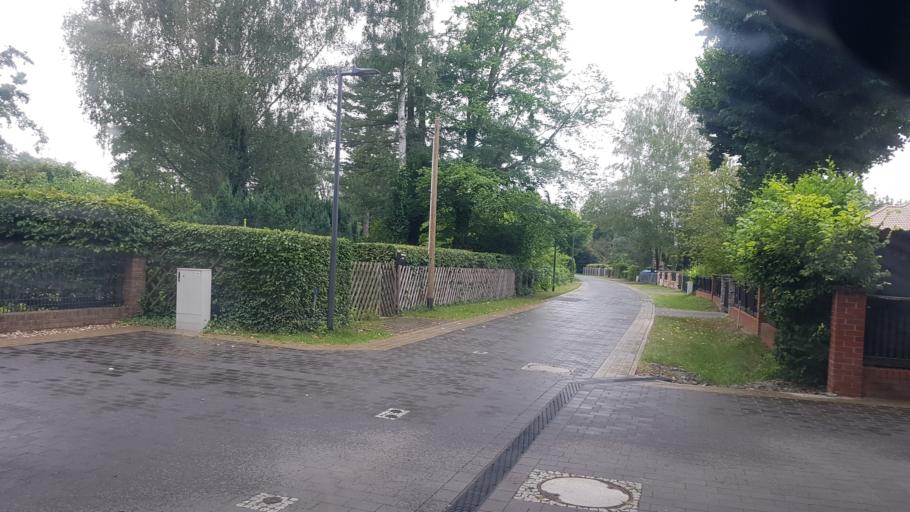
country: DE
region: Brandenburg
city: Teupitz
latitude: 52.1414
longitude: 13.6201
